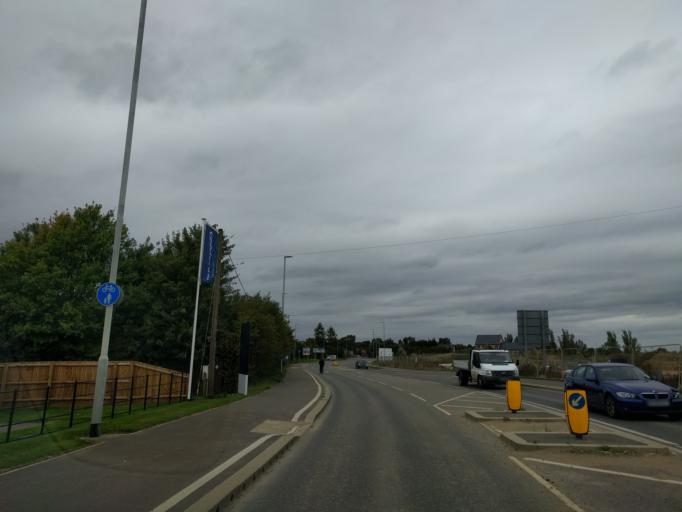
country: GB
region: England
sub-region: Cambridgeshire
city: Swavesey
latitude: 52.2894
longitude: 0.0498
